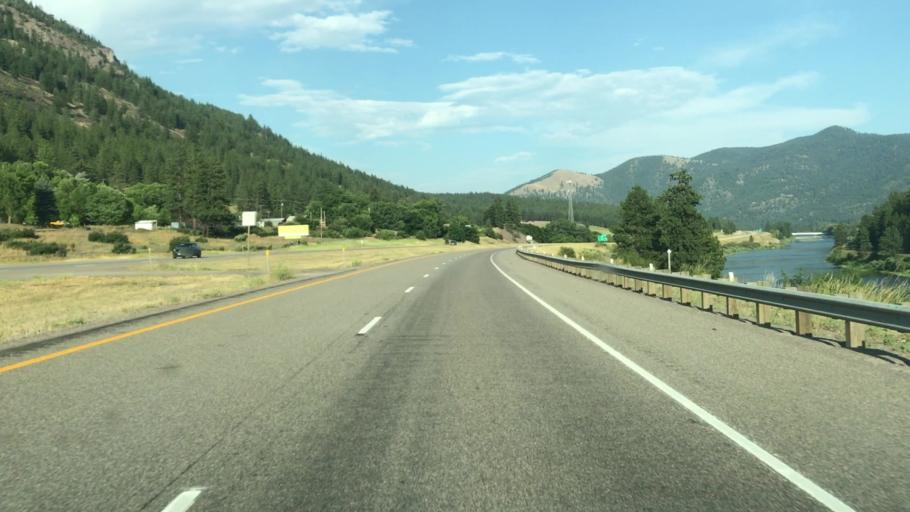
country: US
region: Montana
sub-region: Missoula County
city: Frenchtown
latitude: 47.0008
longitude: -114.4777
